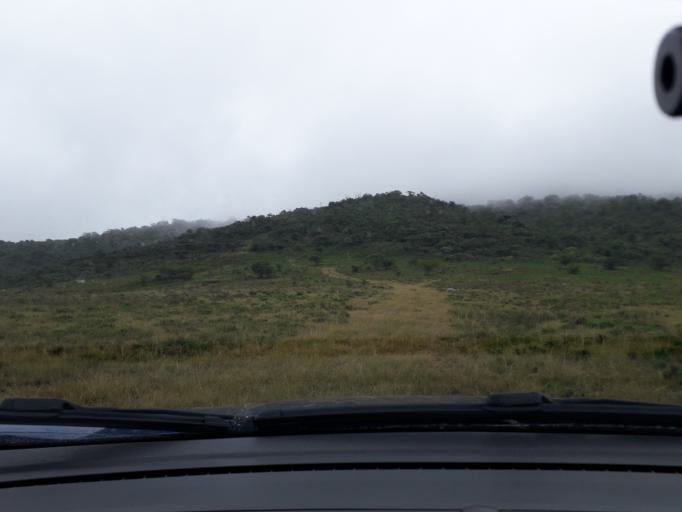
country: ZA
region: Eastern Cape
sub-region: Buffalo City Metropolitan Municipality
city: Bhisho
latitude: -32.7298
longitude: 27.3713
